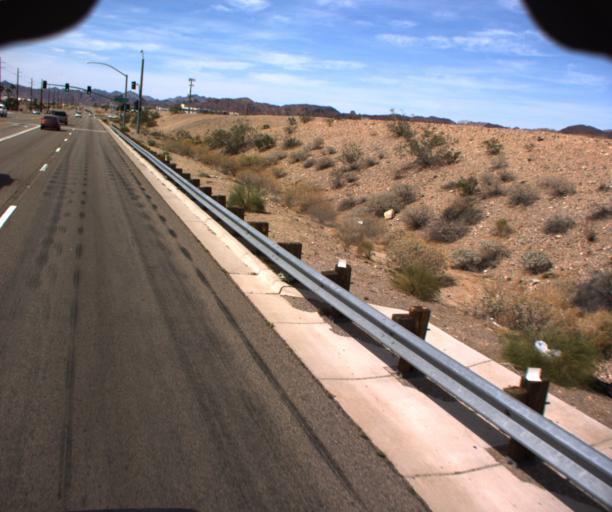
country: US
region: Arizona
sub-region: Mohave County
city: Desert Hills
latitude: 34.5351
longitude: -114.3511
